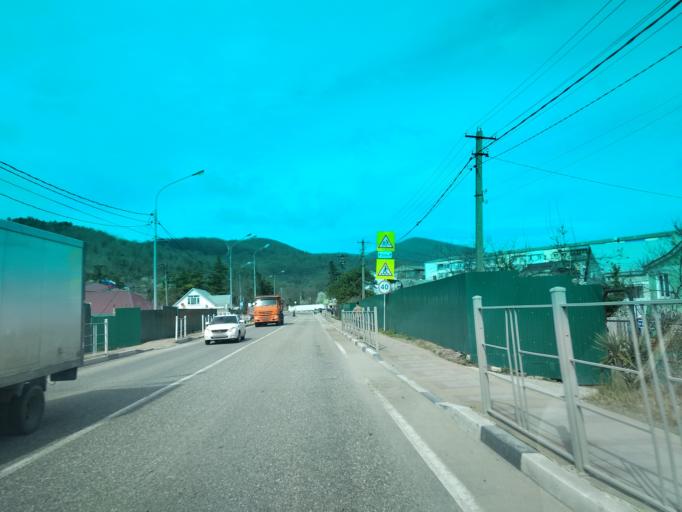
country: RU
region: Krasnodarskiy
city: Shepsi
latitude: 44.0402
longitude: 39.1507
